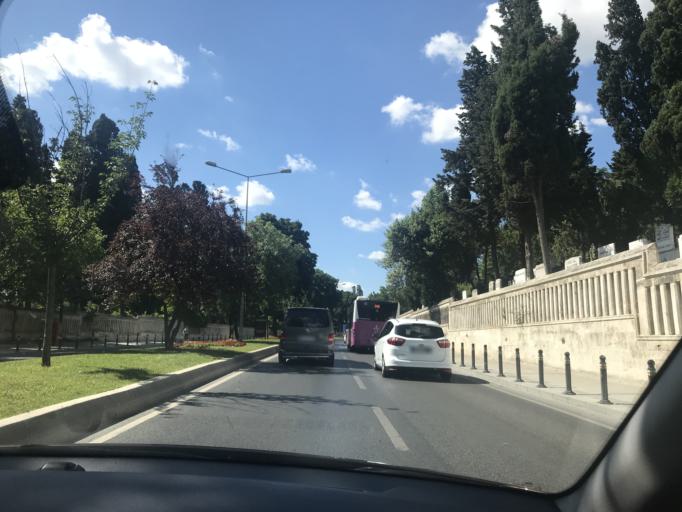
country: TR
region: Istanbul
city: UEskuedar
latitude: 41.0107
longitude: 29.0214
